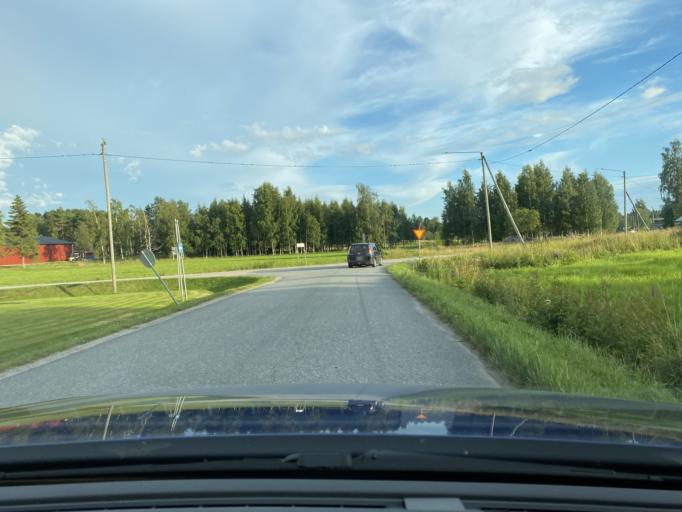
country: FI
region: Ostrobothnia
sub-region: Vaasa
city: Korsnaes
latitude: 62.9654
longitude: 21.1914
